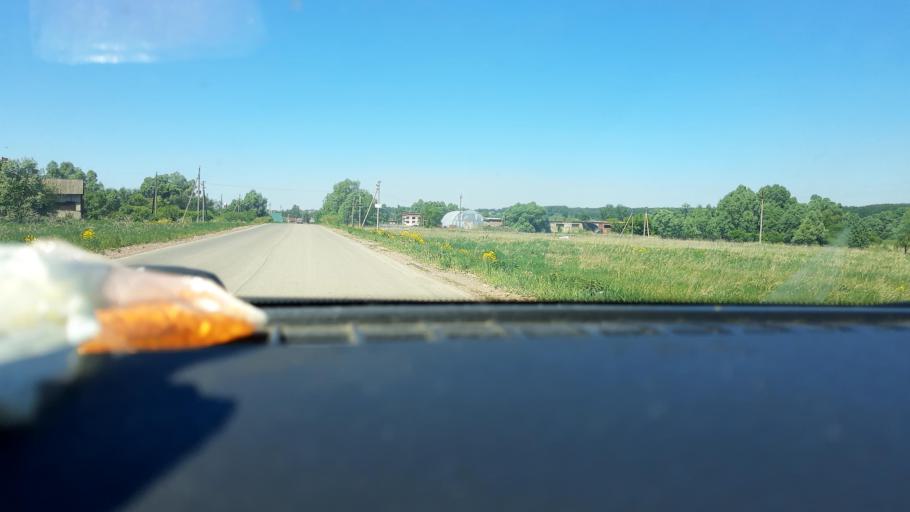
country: RU
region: Bashkortostan
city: Kabakovo
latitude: 54.6955
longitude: 56.2603
